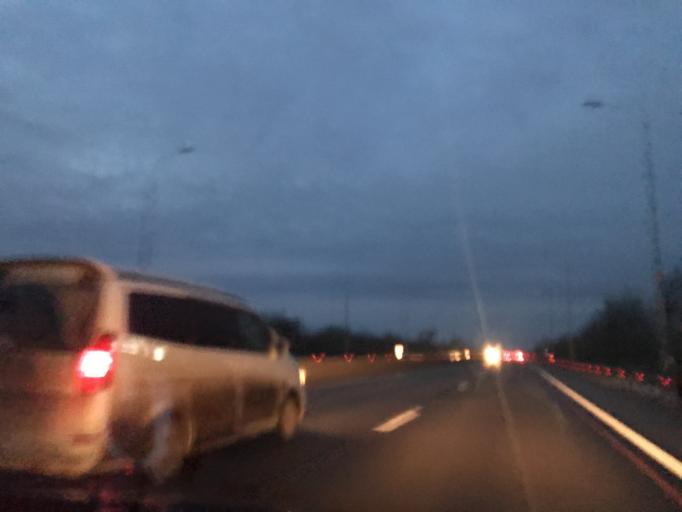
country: RU
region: Rostov
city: Samarskoye
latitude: 47.0304
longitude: 39.7392
